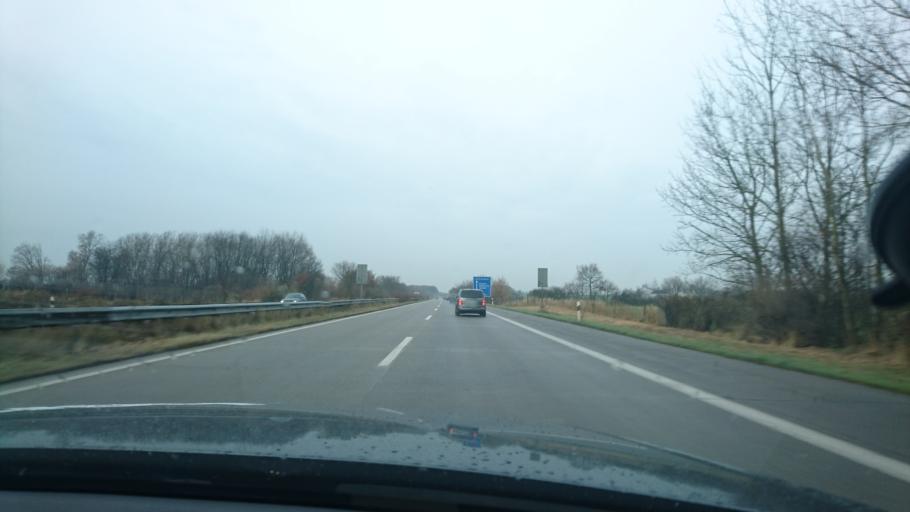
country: DE
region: Schleswig-Holstein
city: Scharbeutz
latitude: 53.9955
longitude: 10.7325
